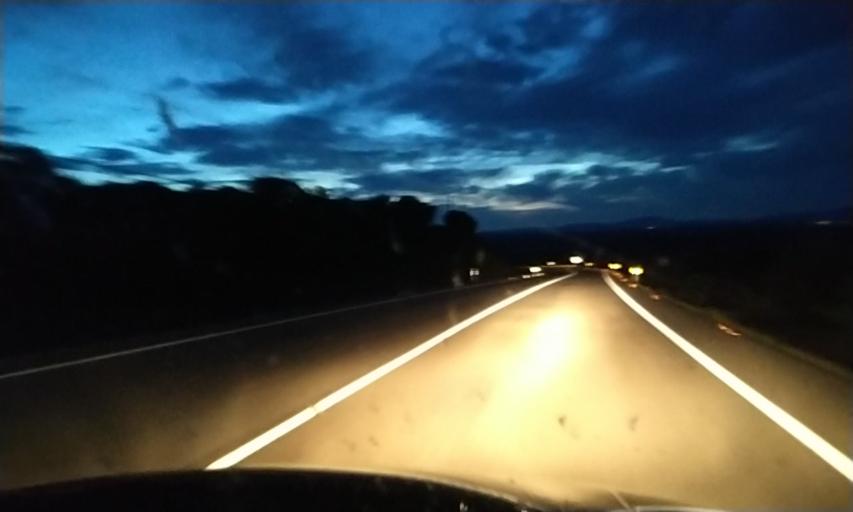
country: ES
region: Extremadura
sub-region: Provincia de Caceres
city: Galisteo
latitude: 39.9778
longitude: -6.2025
